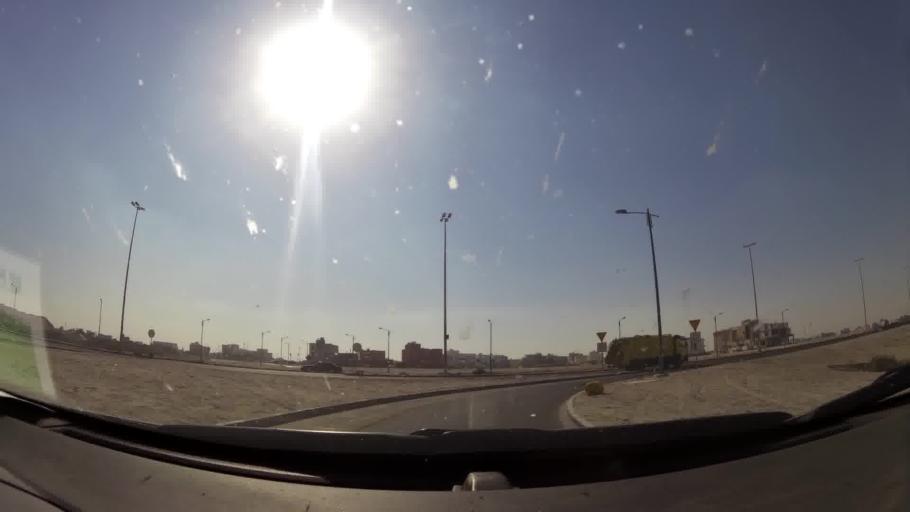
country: SA
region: Eastern Province
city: Al Khafji
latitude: 28.6748
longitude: 48.3593
